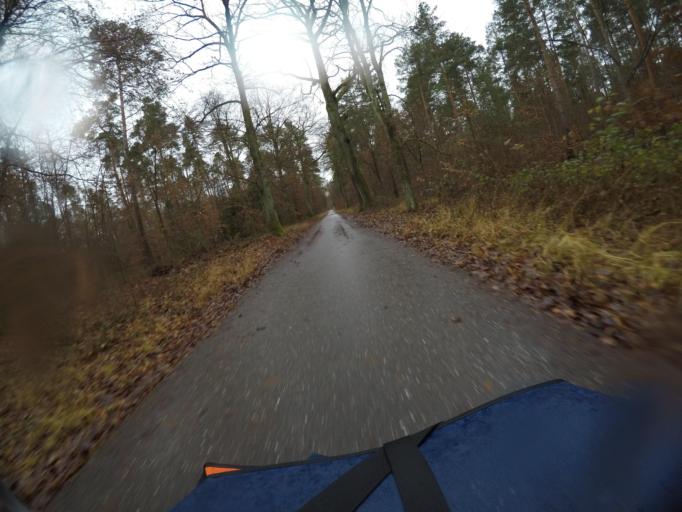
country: DE
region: Baden-Wuerttemberg
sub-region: Karlsruhe Region
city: Eggenstein-Leopoldshafen
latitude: 49.0862
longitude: 8.4588
